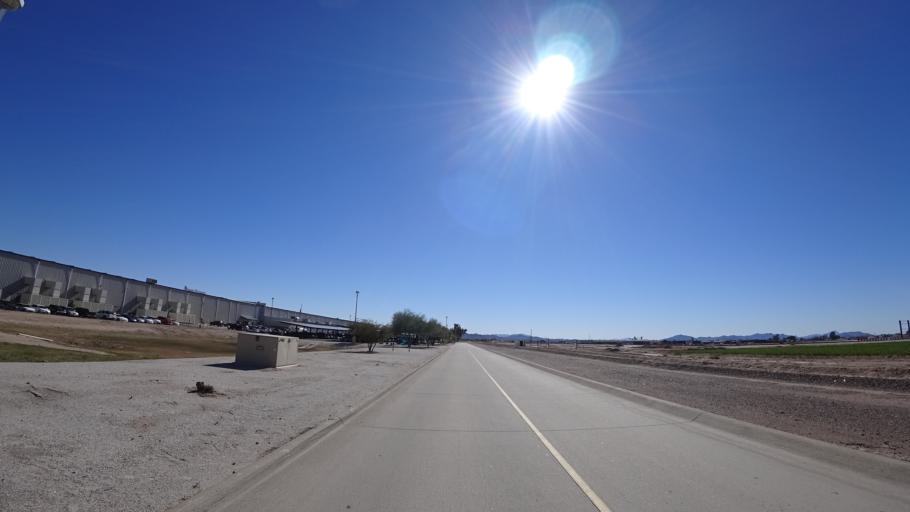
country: US
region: Arizona
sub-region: Maricopa County
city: Buckeye
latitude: 33.3891
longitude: -112.5648
